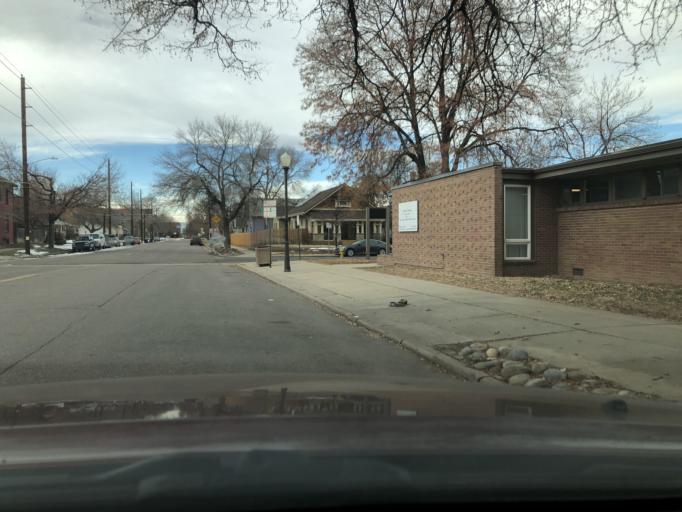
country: US
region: Colorado
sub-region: Denver County
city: Denver
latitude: 39.7571
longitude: -104.9630
